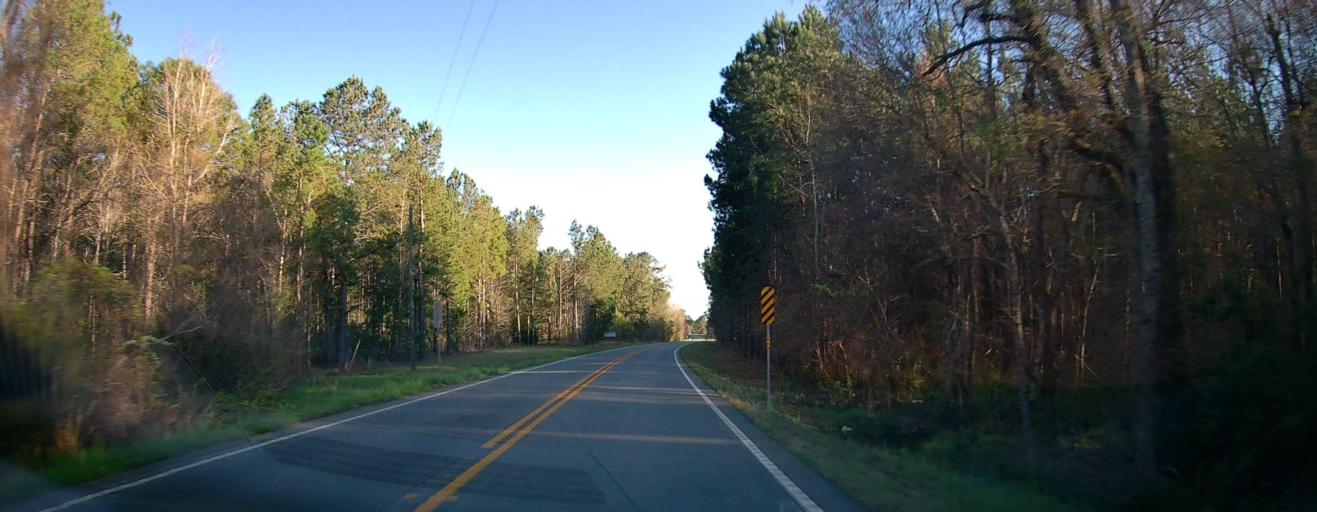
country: US
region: Georgia
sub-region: Pulaski County
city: Hawkinsville
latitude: 32.1967
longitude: -83.3714
